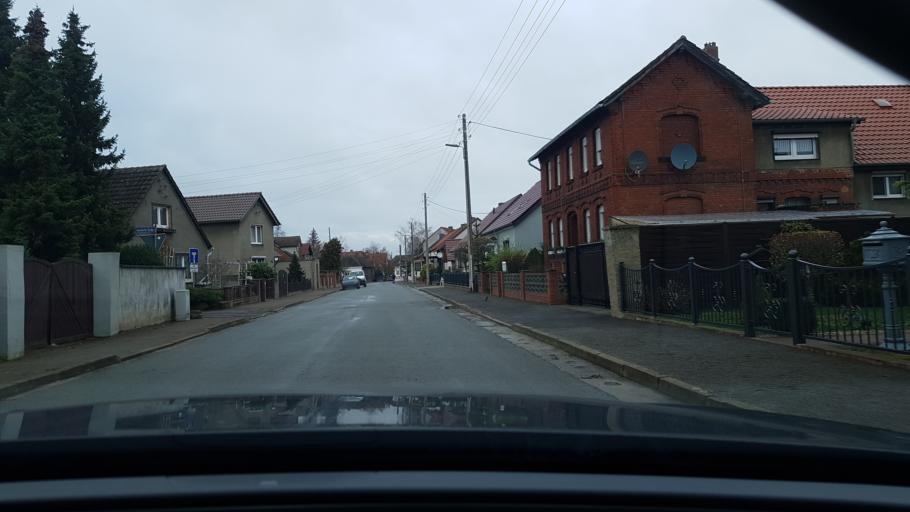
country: DE
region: Saxony-Anhalt
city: Weferlingen
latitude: 52.3984
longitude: 11.1154
